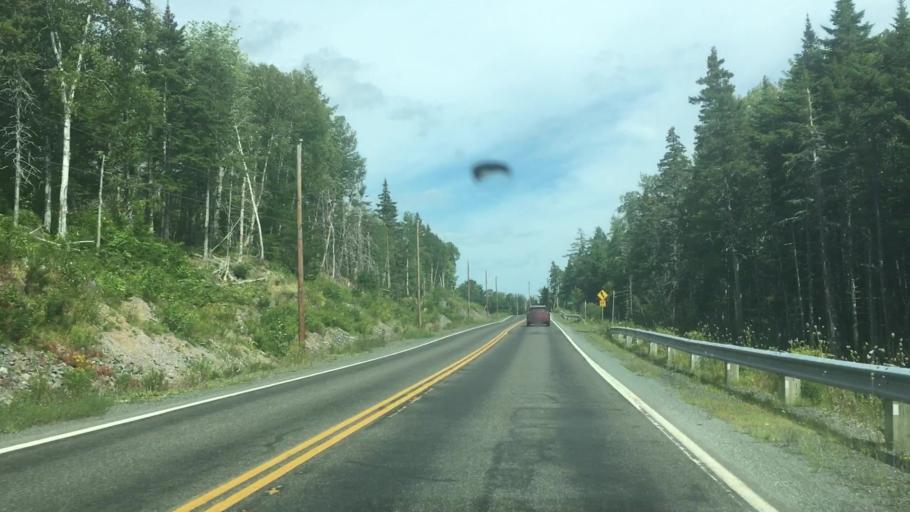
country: CA
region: Nova Scotia
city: Sydney Mines
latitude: 46.2104
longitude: -60.6212
